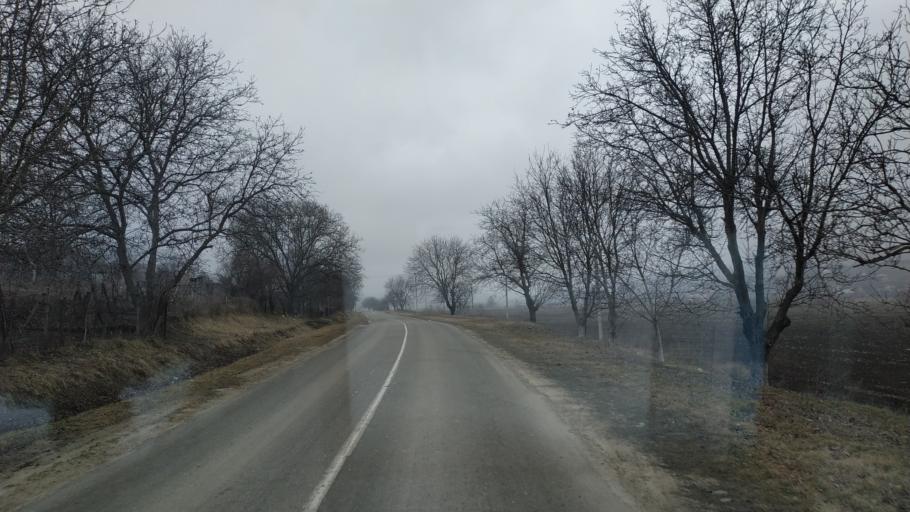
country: MD
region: Hincesti
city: Hincesti
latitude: 46.9604
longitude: 28.4860
